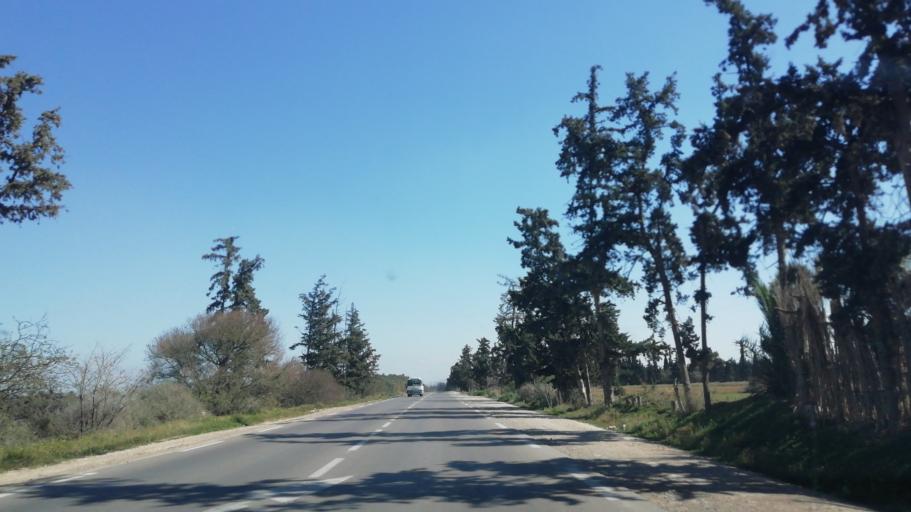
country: DZ
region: Mascara
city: Sig
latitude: 35.5678
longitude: -0.0628
